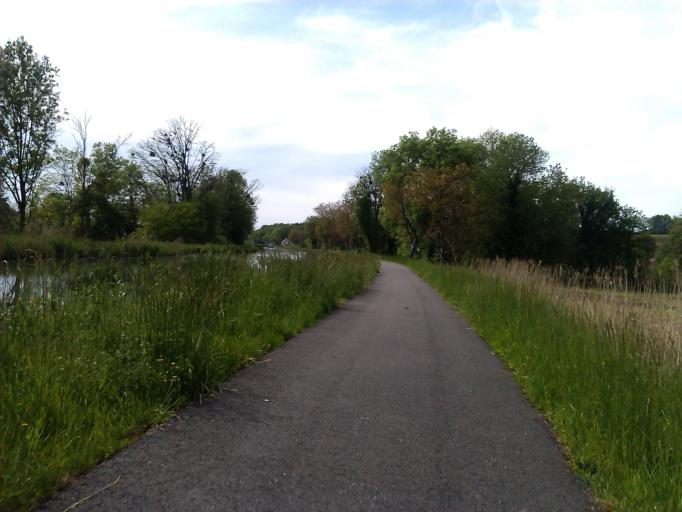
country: FR
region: Franche-Comte
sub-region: Departement du Doubs
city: Saint-Vit
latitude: 47.1652
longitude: 5.8485
